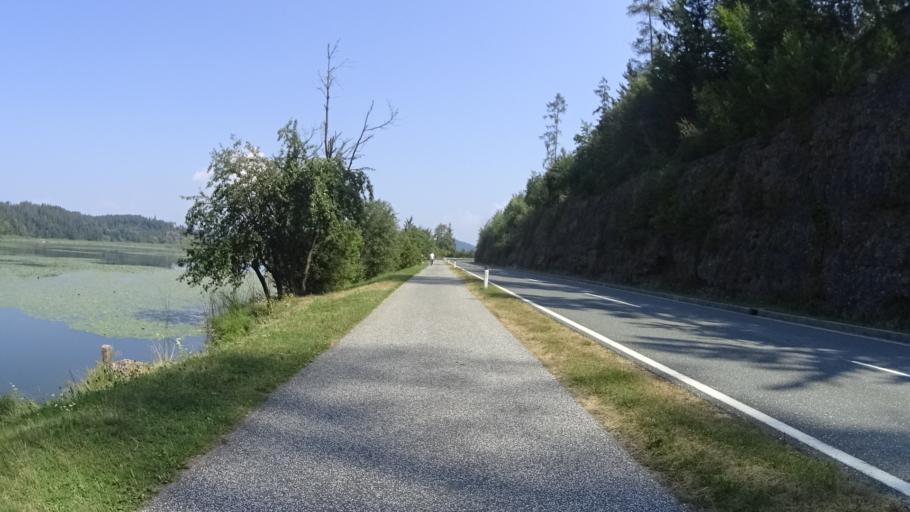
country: AT
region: Carinthia
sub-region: Politischer Bezirk Volkermarkt
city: Sittersdorf
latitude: 46.5616
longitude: 14.6242
